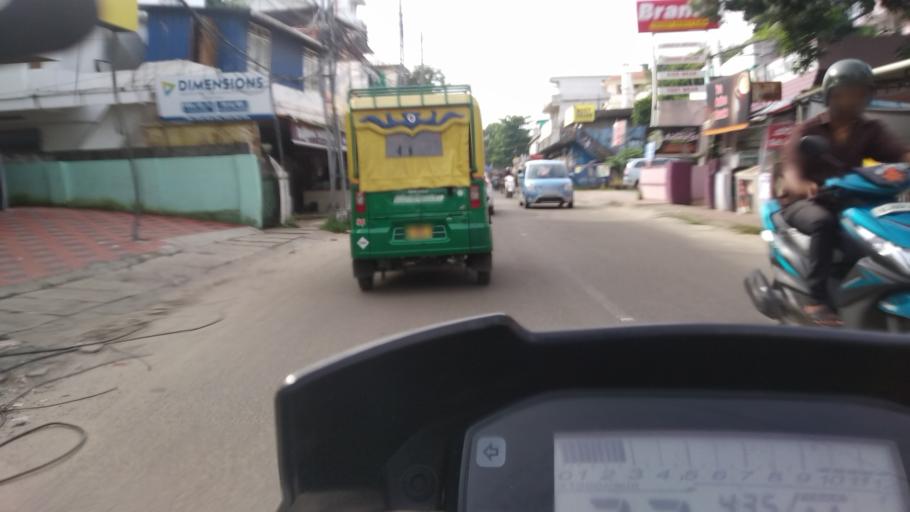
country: IN
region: Kerala
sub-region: Ernakulam
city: Cochin
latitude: 9.9850
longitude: 76.3115
